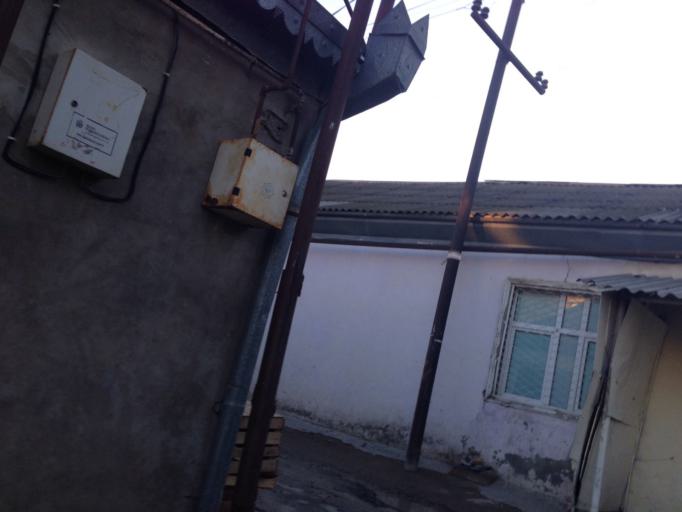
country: AZ
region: Baki
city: Baku
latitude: 40.4169
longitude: 49.8649
